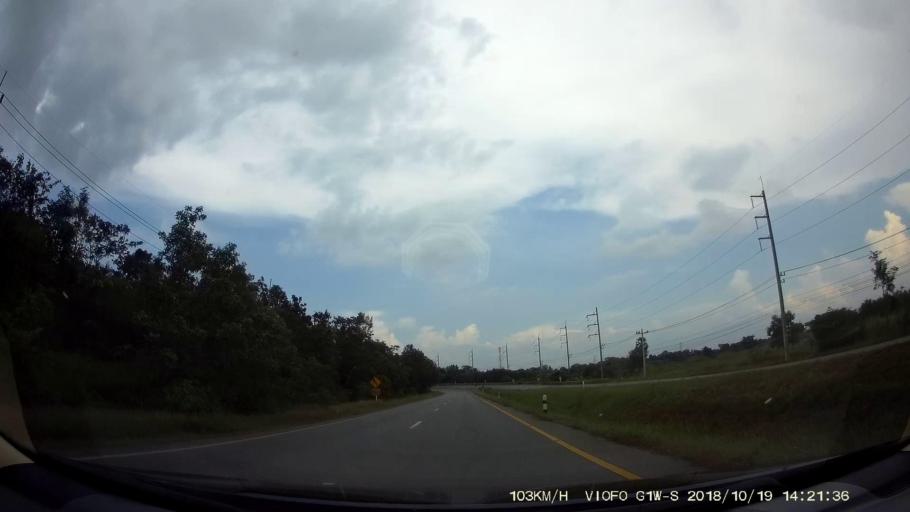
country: TH
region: Chaiyaphum
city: Kaeng Khro
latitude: 16.0538
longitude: 102.2686
